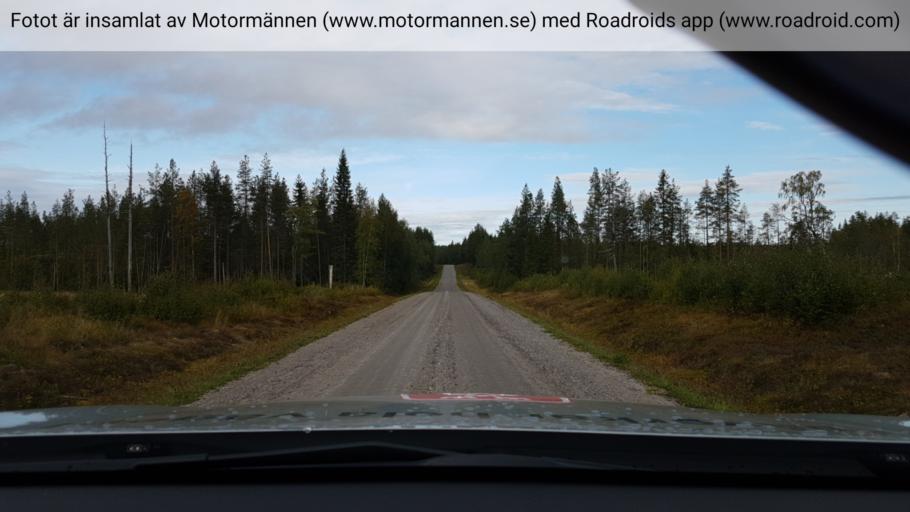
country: SE
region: Vaesterbotten
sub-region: Skelleftea Kommun
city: Byske
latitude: 65.1367
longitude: 21.1878
